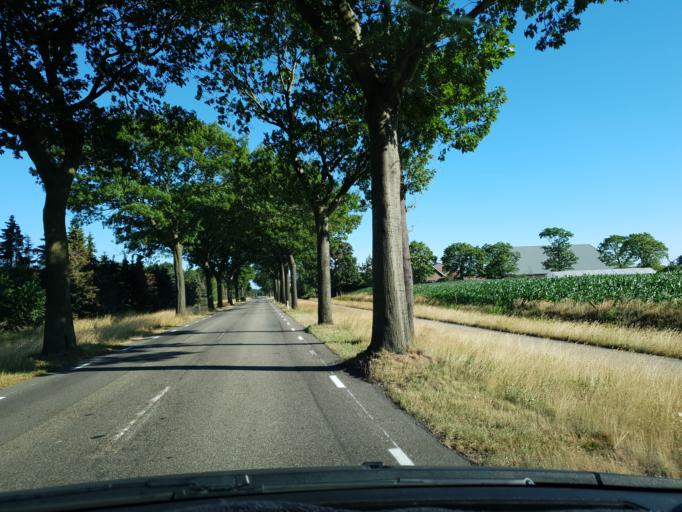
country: NL
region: North Brabant
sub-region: Gemeente Rucphen
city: Rucphen
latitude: 51.5036
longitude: 4.5849
